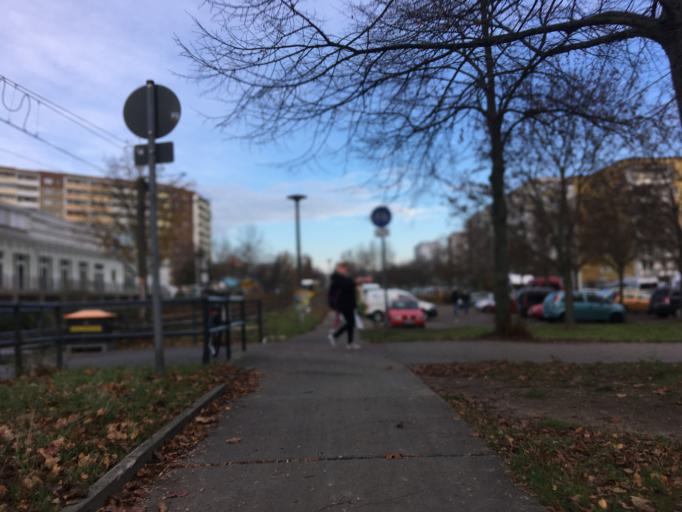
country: DE
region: Brandenburg
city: Ahrensfelde
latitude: 52.5650
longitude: 13.5720
